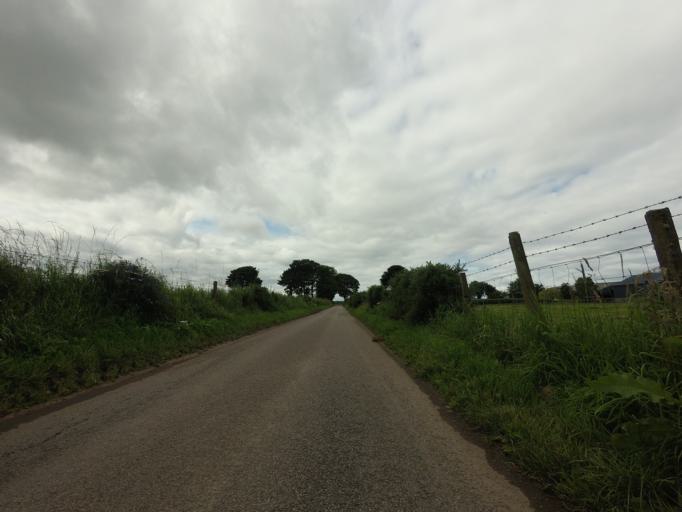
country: GB
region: Scotland
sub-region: Moray
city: Kinloss
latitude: 57.6325
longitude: -3.5320
